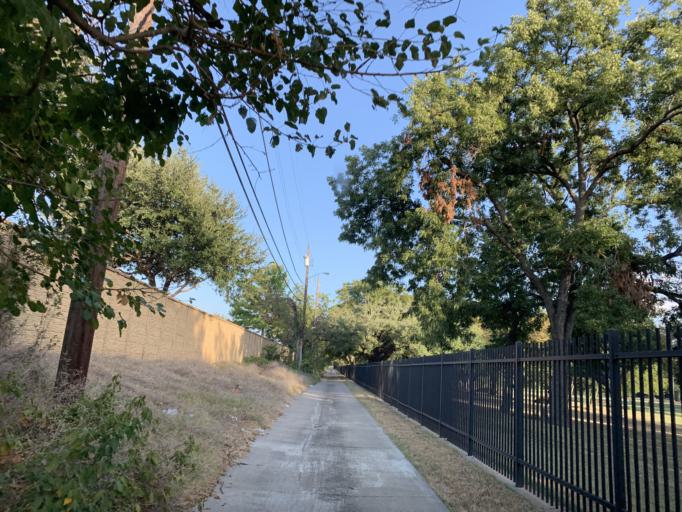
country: US
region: Texas
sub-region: Dallas County
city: Dallas
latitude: 32.7579
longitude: -96.7493
